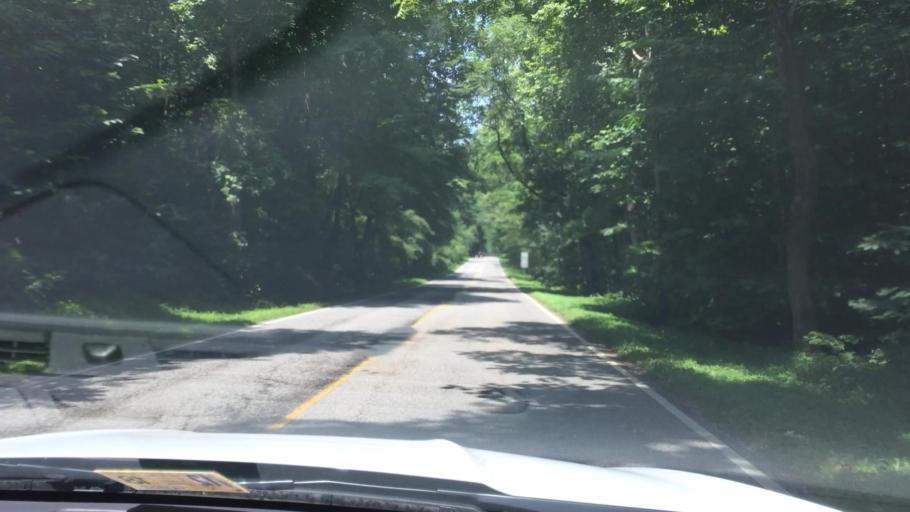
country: US
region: Virginia
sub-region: York County
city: Yorktown
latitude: 37.2096
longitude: -76.4995
